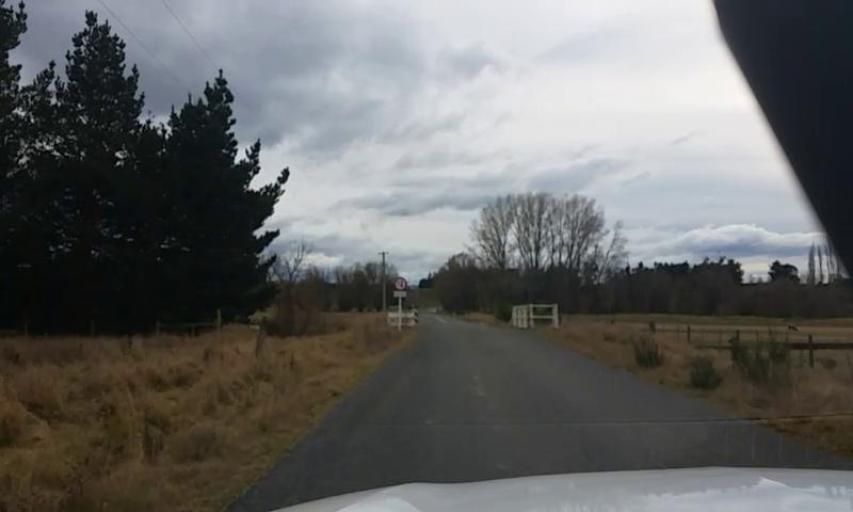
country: NZ
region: Canterbury
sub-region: Waimakariri District
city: Kaiapoi
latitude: -43.3044
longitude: 172.4380
